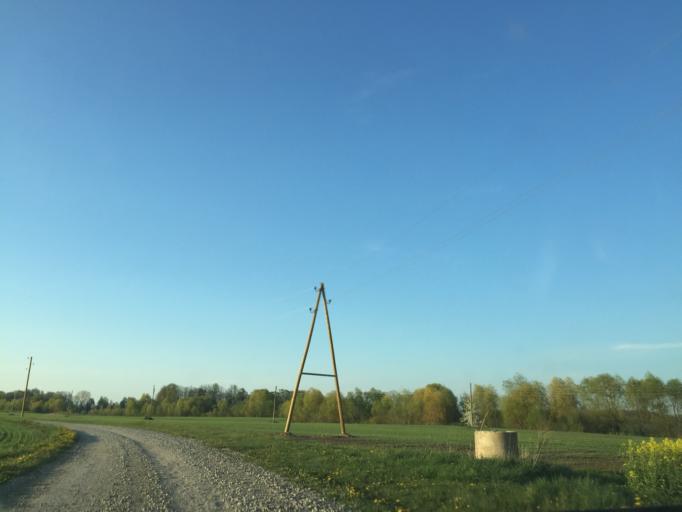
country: LV
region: Bauskas Rajons
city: Bauska
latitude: 56.3098
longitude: 24.1812
